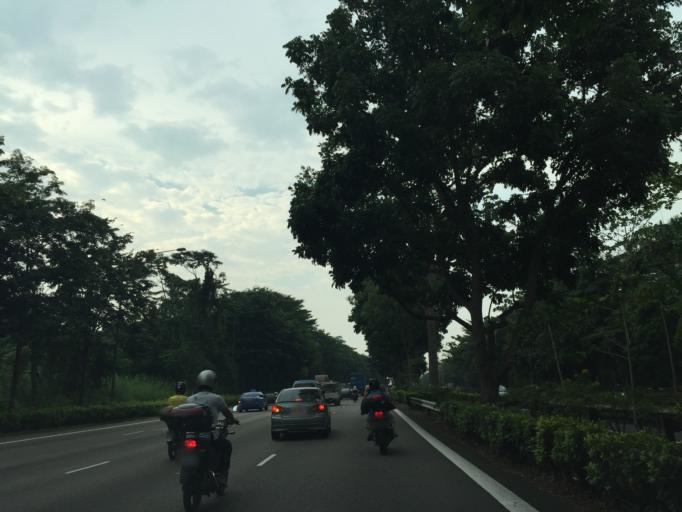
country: MY
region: Johor
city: Johor Bahru
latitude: 1.3936
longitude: 103.7740
